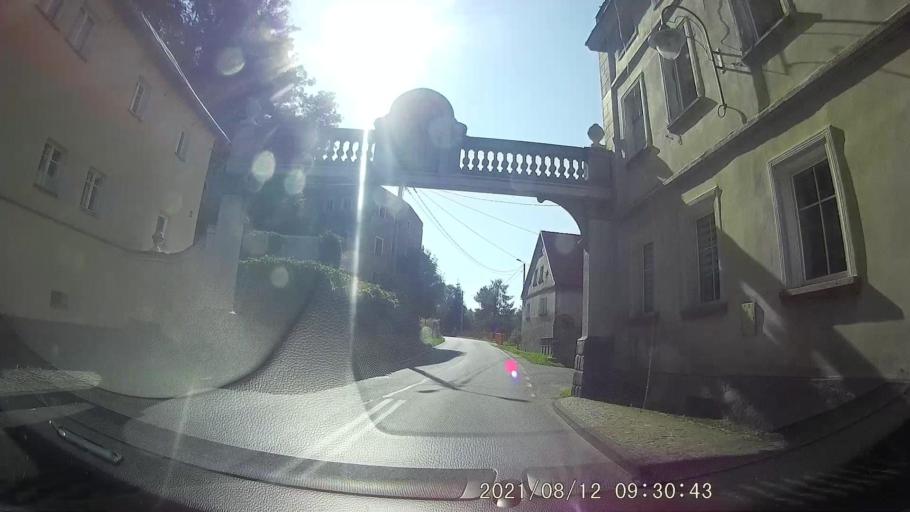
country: PL
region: Lower Silesian Voivodeship
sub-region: Powiat klodzki
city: Radkow
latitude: 50.4891
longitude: 16.4572
